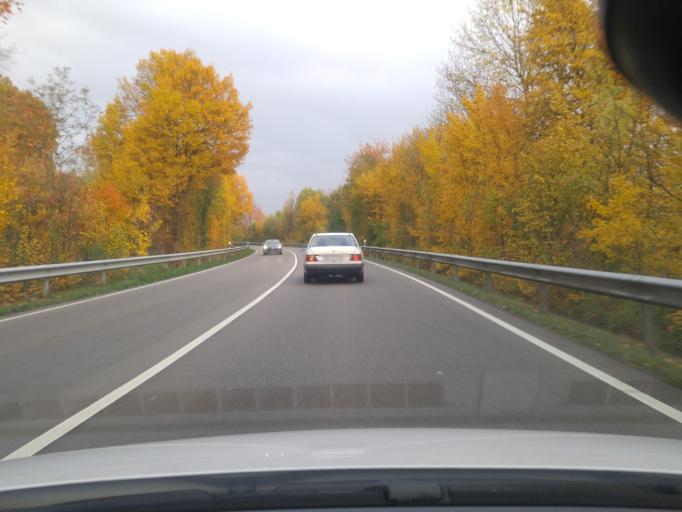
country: DE
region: Baden-Wuerttemberg
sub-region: Karlsruhe Region
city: Balzfeld
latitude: 49.2421
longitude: 8.7960
